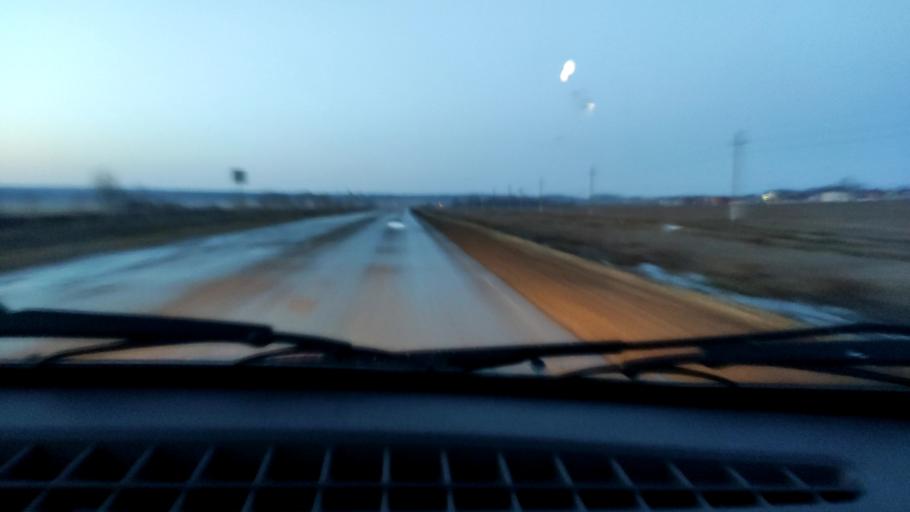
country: RU
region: Bashkortostan
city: Iglino
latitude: 54.7974
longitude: 56.4148
